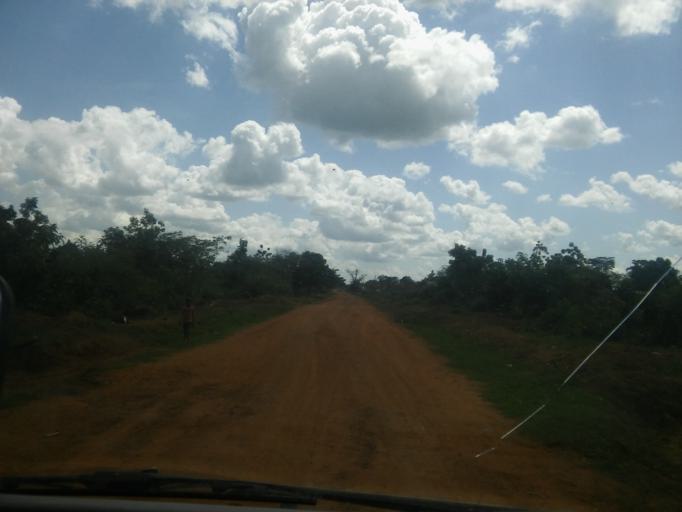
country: UG
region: Eastern Region
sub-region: Pallisa District
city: Pallisa
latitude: 1.1550
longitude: 33.7979
